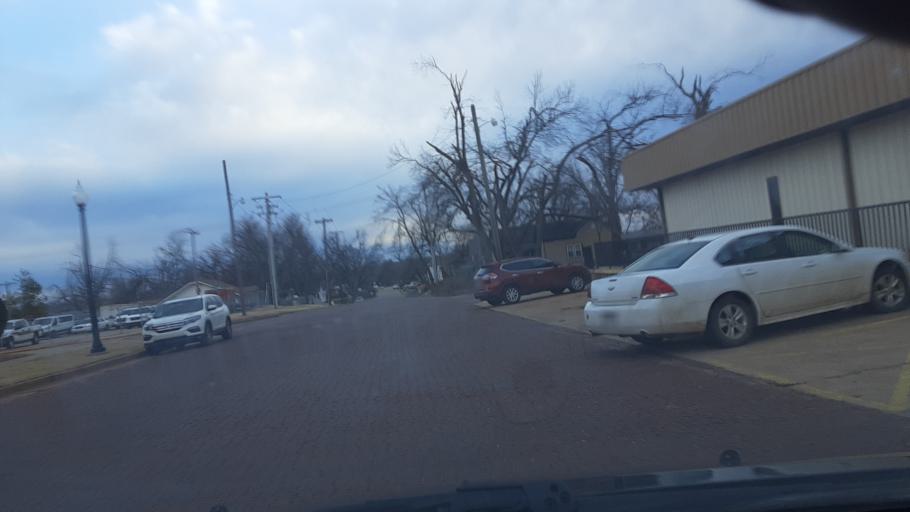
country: US
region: Oklahoma
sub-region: Logan County
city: Guthrie
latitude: 35.8763
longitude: -97.4228
